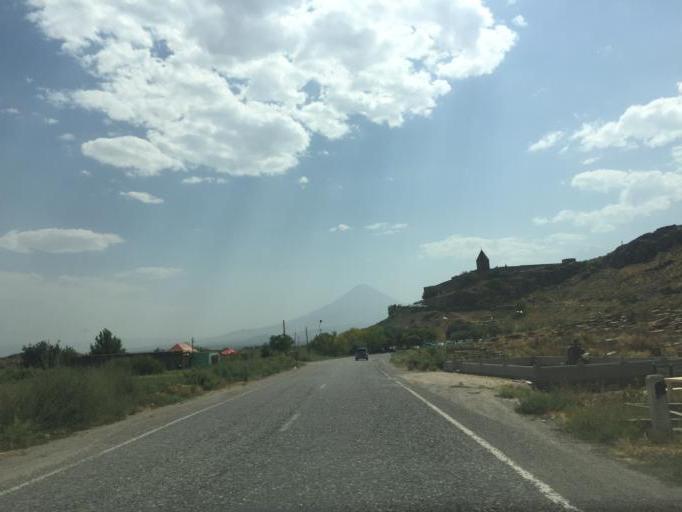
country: AM
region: Ararat
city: Shahumyan
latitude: 39.8806
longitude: 44.5787
